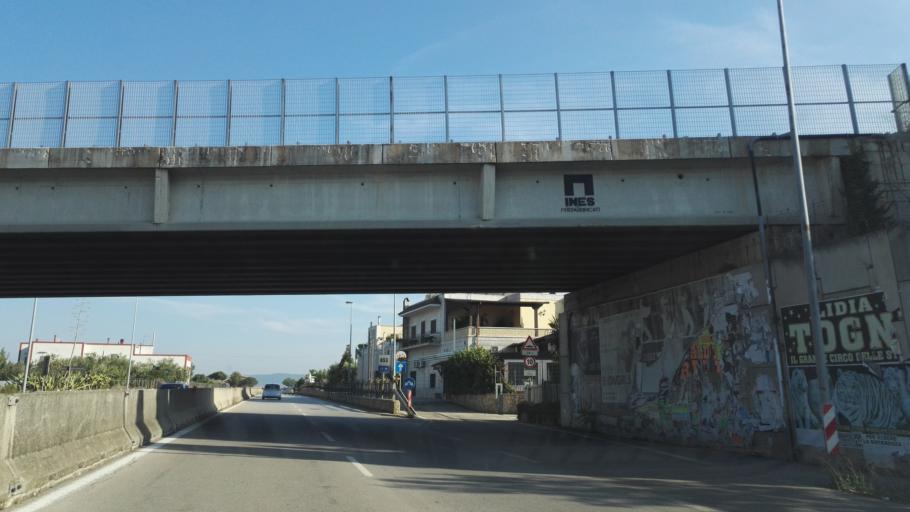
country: IT
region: Apulia
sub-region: Provincia di Brindisi
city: Fasano
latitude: 40.8806
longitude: 17.3381
